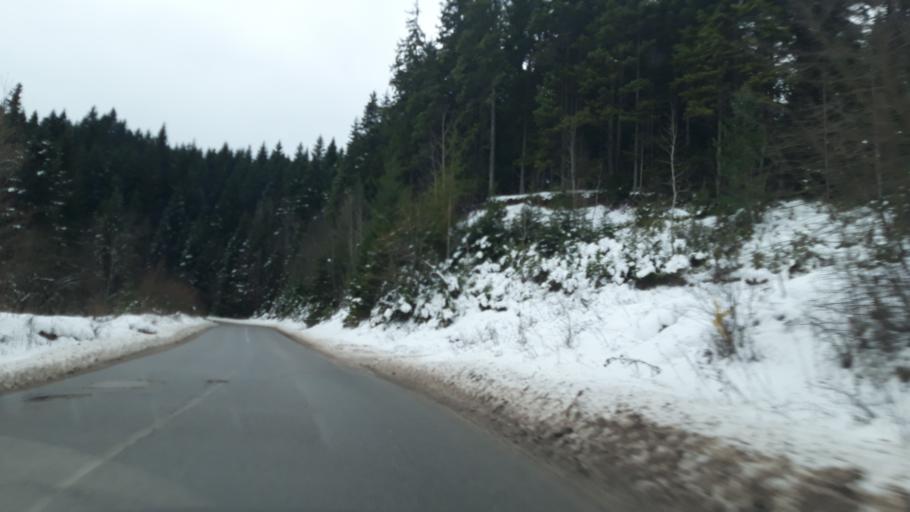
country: BA
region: Republika Srpska
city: Koran
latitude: 43.8028
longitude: 18.5482
